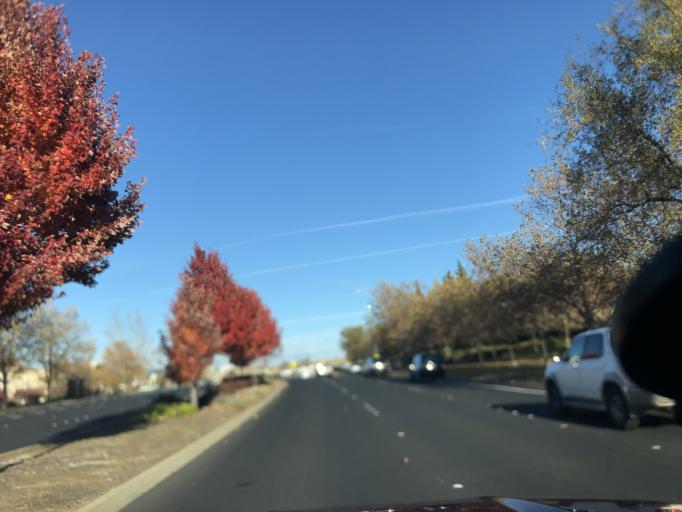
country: US
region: California
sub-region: Placer County
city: Roseville
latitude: 38.7768
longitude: -121.2897
